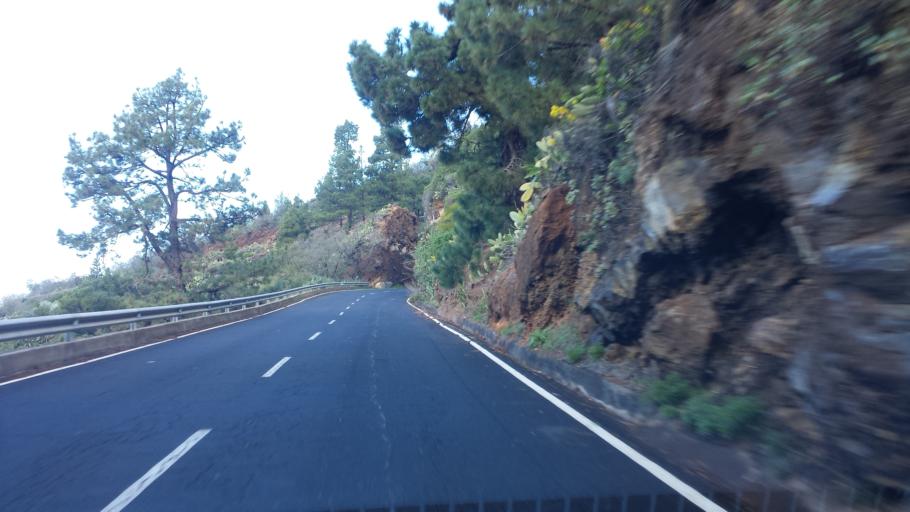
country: ES
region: Canary Islands
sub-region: Provincia de Santa Cruz de Tenerife
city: Puntagorda
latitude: 28.7396
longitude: -17.9649
